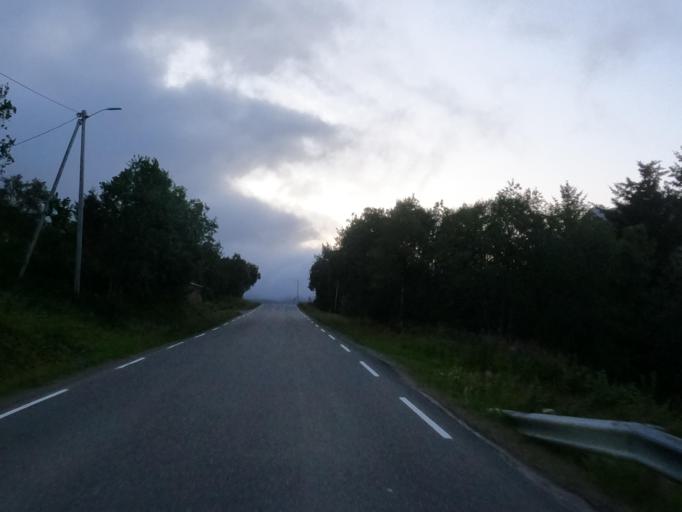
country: NO
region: Nordland
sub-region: Lodingen
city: Lodingen
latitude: 68.5781
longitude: 15.7930
